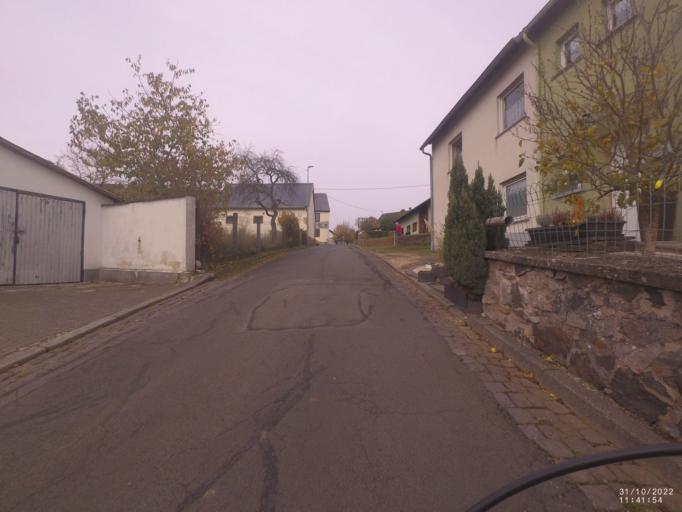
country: DE
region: Rheinland-Pfalz
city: Kradenbach
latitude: 50.2554
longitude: 6.8541
